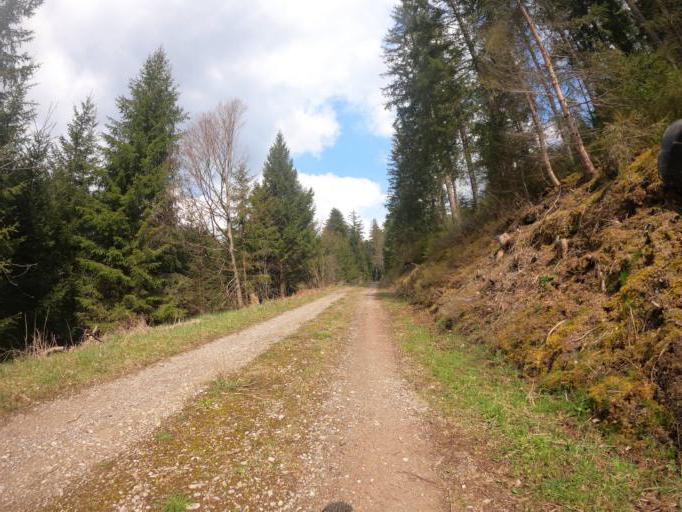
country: DE
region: Baden-Wuerttemberg
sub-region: Karlsruhe Region
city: Schomberg
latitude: 48.7707
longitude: 8.6229
